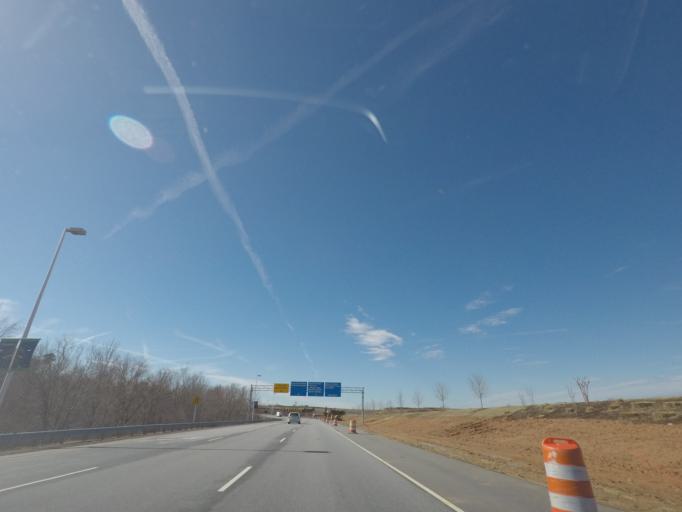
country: US
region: North Carolina
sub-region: Guilford County
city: Oak Ridge
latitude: 36.1083
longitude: -79.9422
